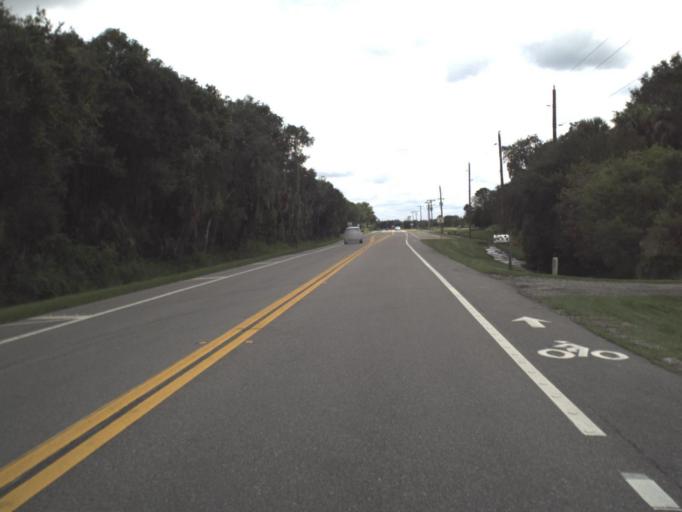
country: US
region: Florida
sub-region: Sarasota County
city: Lake Sarasota
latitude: 27.2490
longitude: -82.3845
